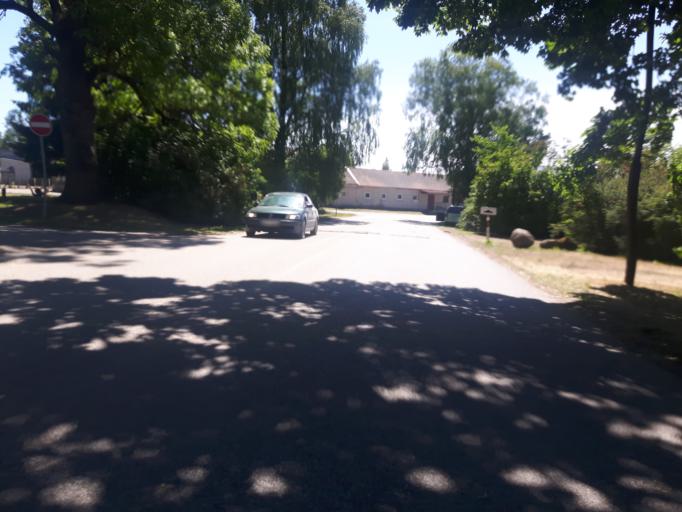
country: LV
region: Grobina
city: Grobina
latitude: 56.5313
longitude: 21.1564
